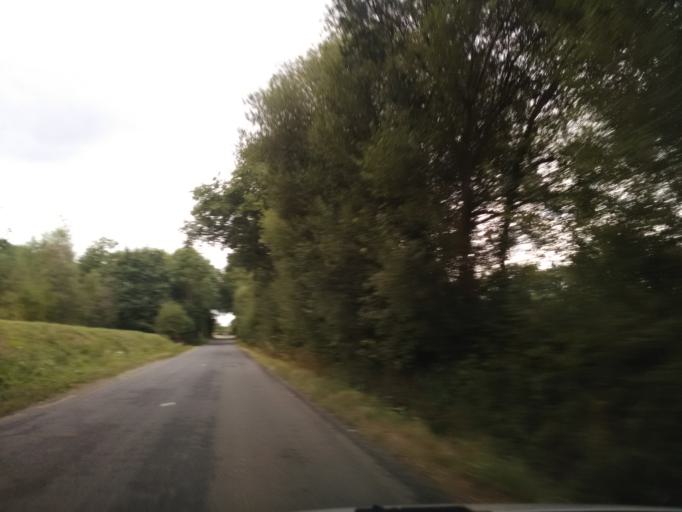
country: FR
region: Brittany
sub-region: Departement d'Ille-et-Vilaine
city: Quebriac
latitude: 48.3516
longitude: -1.7758
